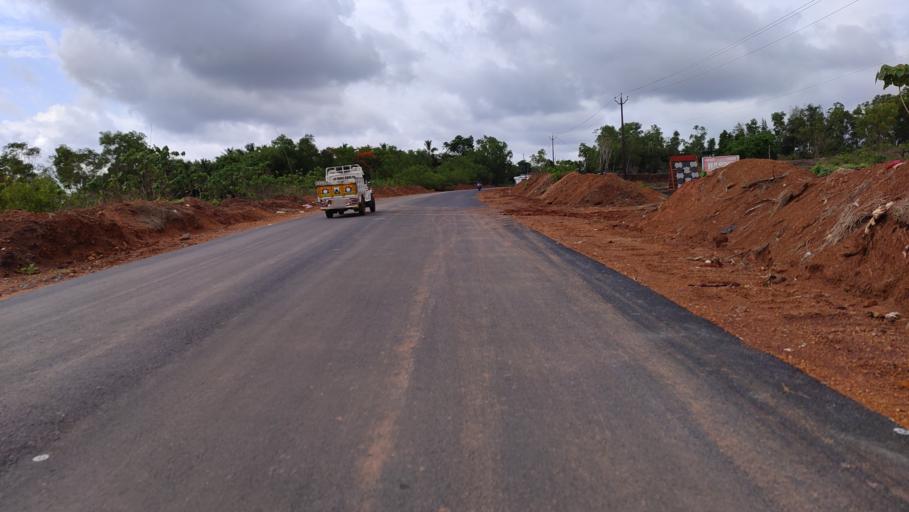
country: IN
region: Kerala
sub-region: Kasaragod District
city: Kasaragod
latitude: 12.5546
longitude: 75.0705
